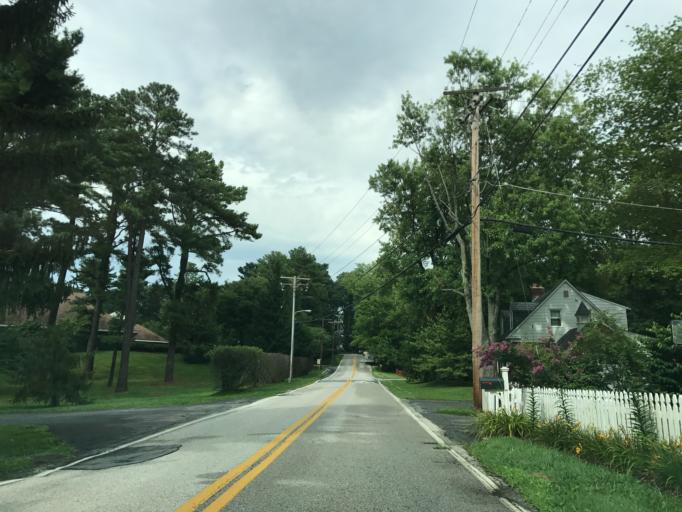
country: US
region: Maryland
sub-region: Baltimore County
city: Lutherville
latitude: 39.4071
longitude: -76.6217
